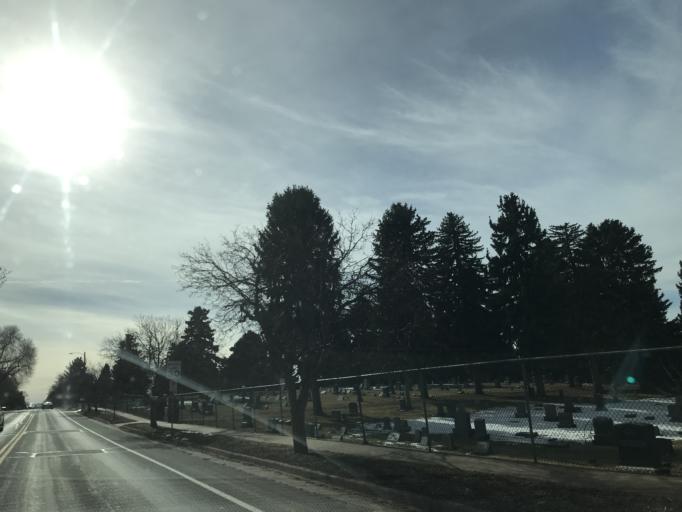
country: US
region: Colorado
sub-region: Arapahoe County
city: Littleton
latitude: 39.6051
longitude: -105.0163
